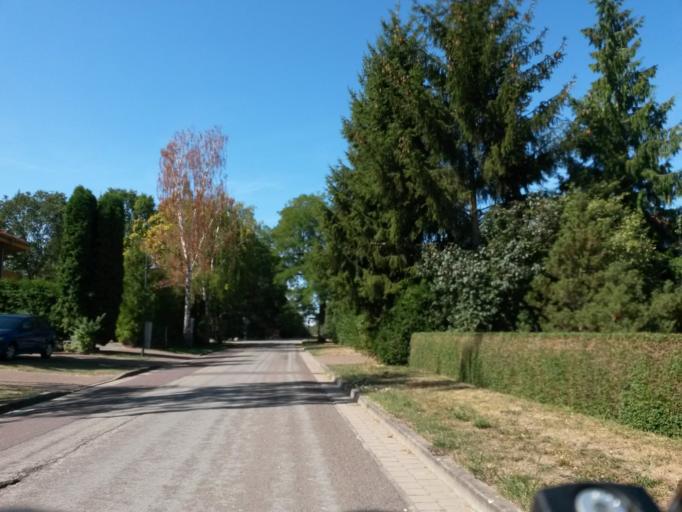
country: DE
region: Saxony-Anhalt
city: Hassel
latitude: 52.6398
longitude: 11.9602
